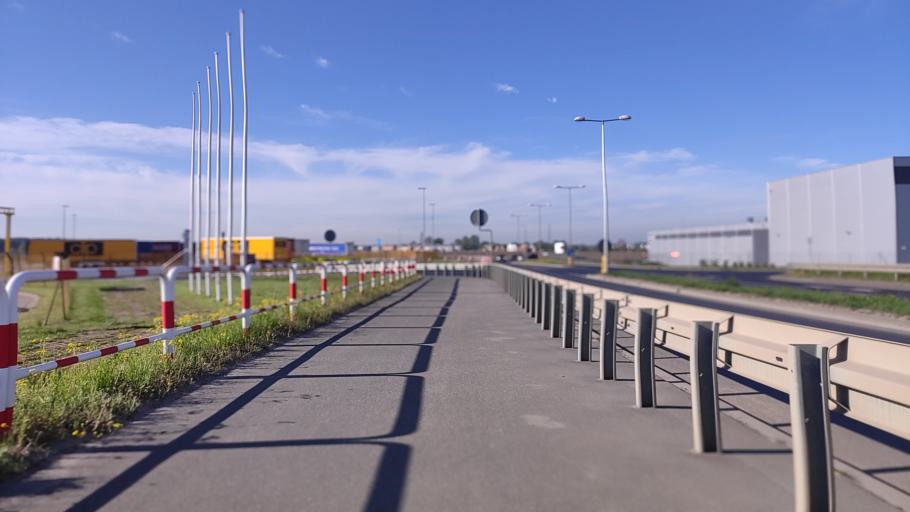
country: PL
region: Greater Poland Voivodeship
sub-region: Powiat poznanski
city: Swarzedz
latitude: 52.3989
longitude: 17.1216
